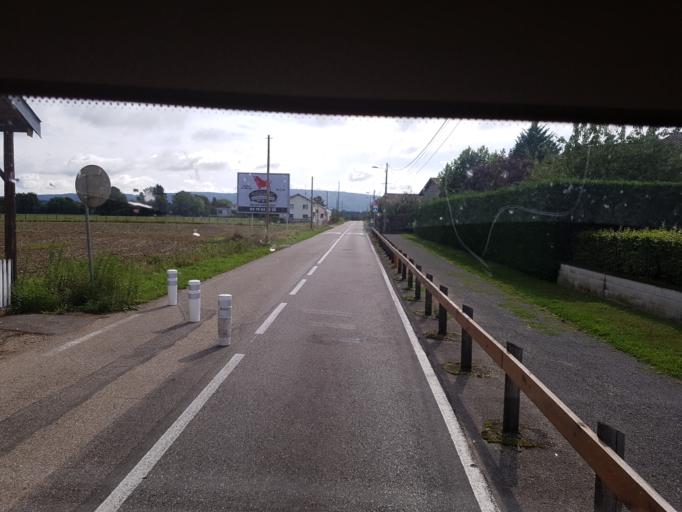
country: FR
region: Rhone-Alpes
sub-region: Departement de l'Ain
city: Bourg-en-Bresse
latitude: 46.1915
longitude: 5.2491
